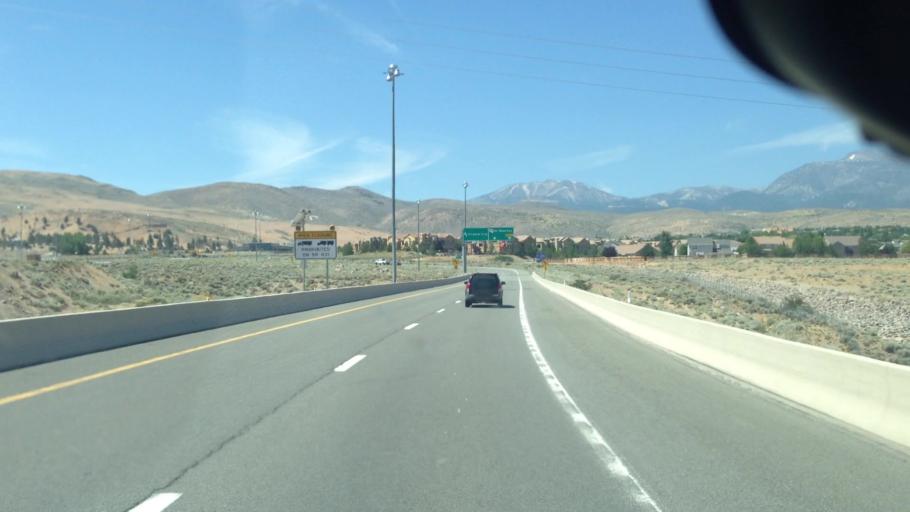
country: US
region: Nevada
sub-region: Washoe County
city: Sparks
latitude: 39.3998
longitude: -119.7582
